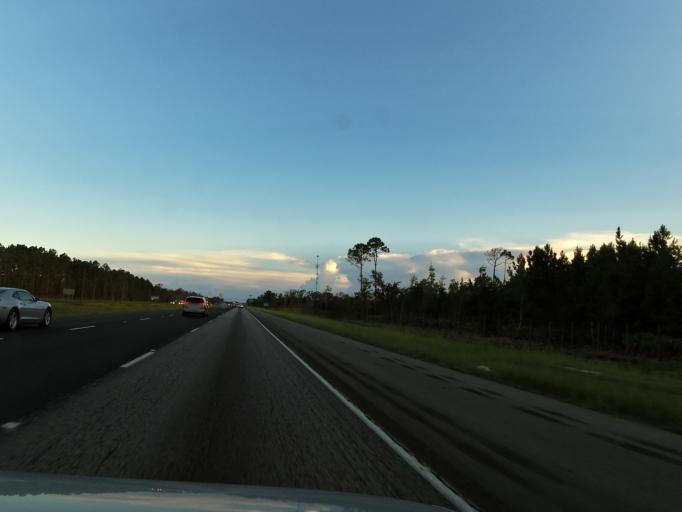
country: US
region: Georgia
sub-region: Camden County
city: Kingsland
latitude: 30.7827
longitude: -81.6576
